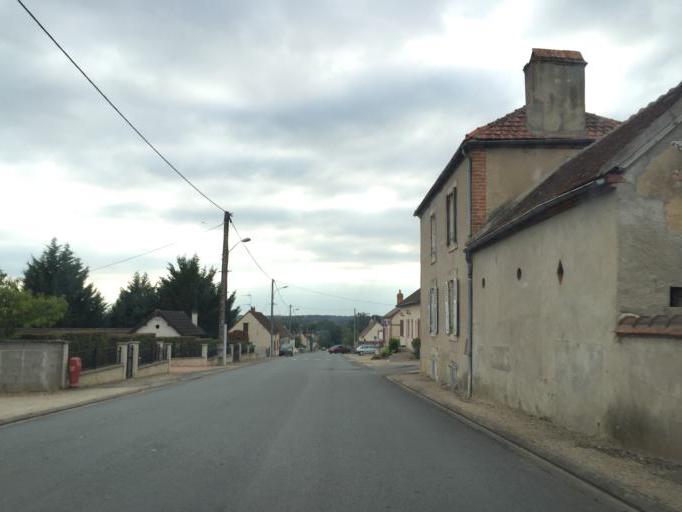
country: FR
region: Auvergne
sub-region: Departement de l'Allier
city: Lusigny
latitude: 46.5286
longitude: 3.4896
